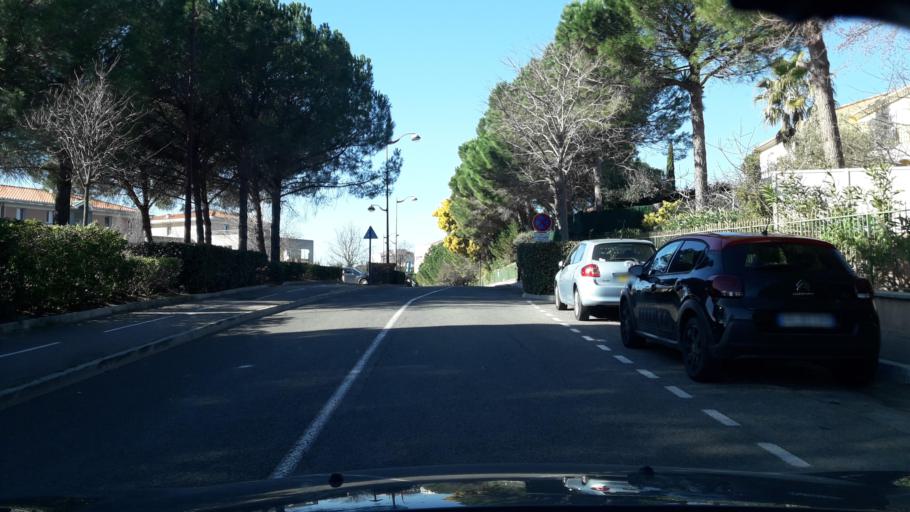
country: FR
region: Provence-Alpes-Cote d'Azur
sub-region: Departement du Var
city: Frejus
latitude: 43.4411
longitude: 6.7514
